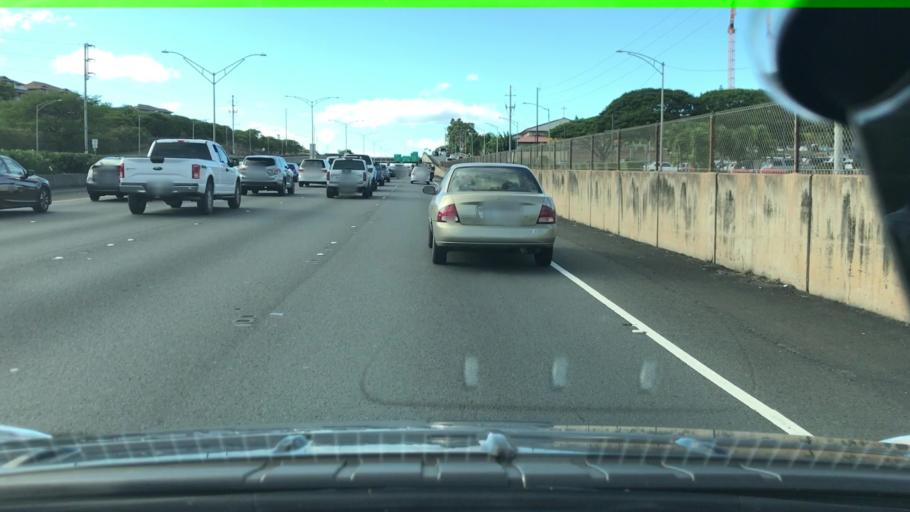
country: US
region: Hawaii
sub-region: Honolulu County
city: Halawa Heights
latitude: 21.3629
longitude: -157.9009
